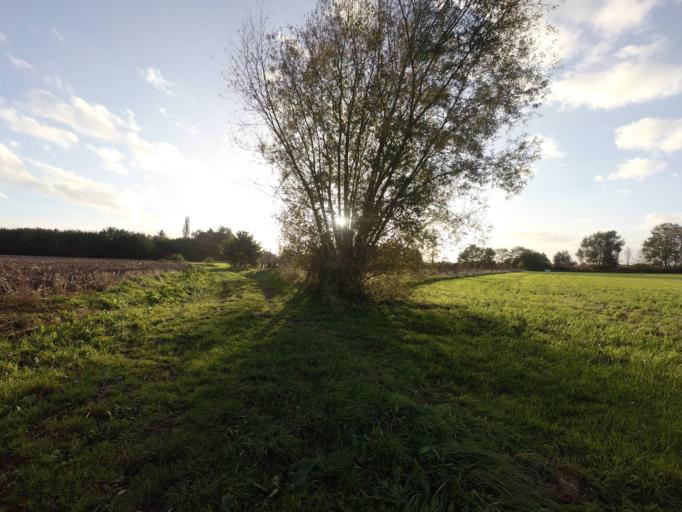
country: BE
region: Flanders
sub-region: Provincie Vlaams-Brabant
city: Zemst
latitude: 50.9804
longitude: 4.4125
